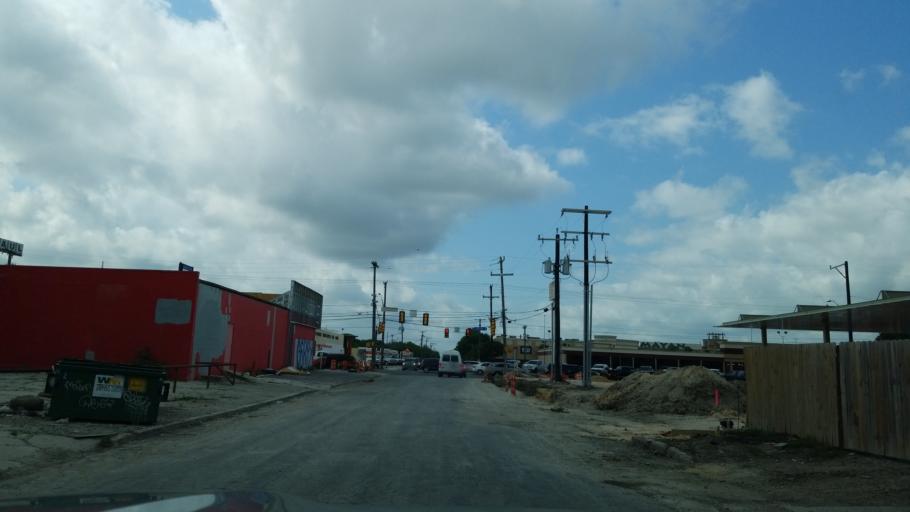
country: US
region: Texas
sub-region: Bexar County
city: San Antonio
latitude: 29.3575
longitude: -98.5231
